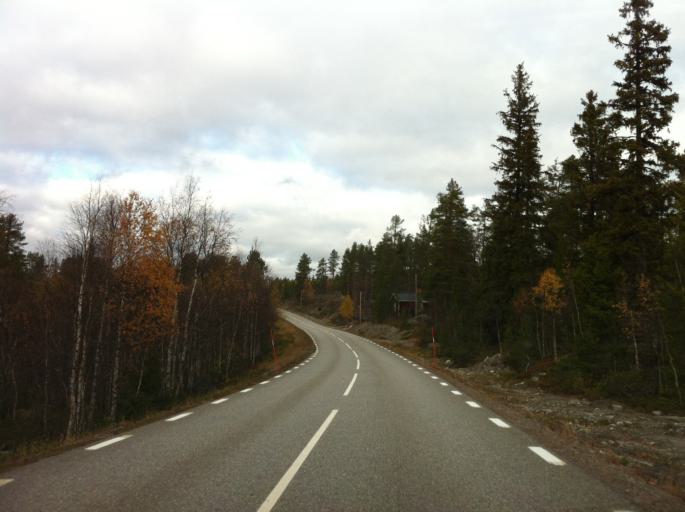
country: NO
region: Hedmark
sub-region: Engerdal
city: Engerdal
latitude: 62.0049
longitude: 12.4146
